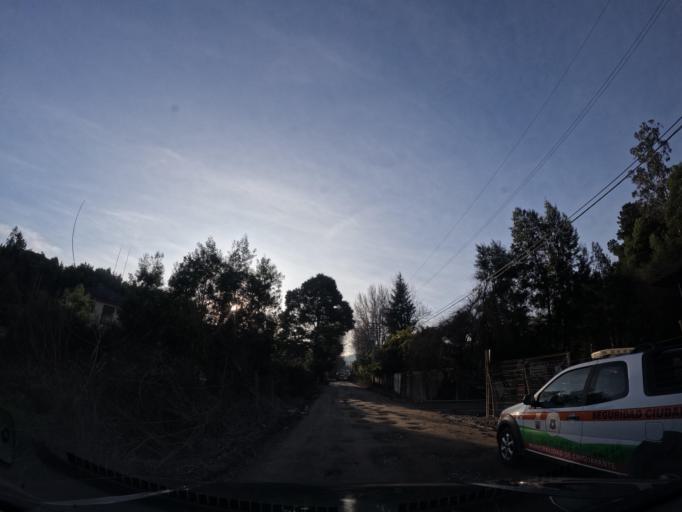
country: CL
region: Biobio
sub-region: Provincia de Concepcion
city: Concepcion
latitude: -36.8550
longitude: -73.0041
